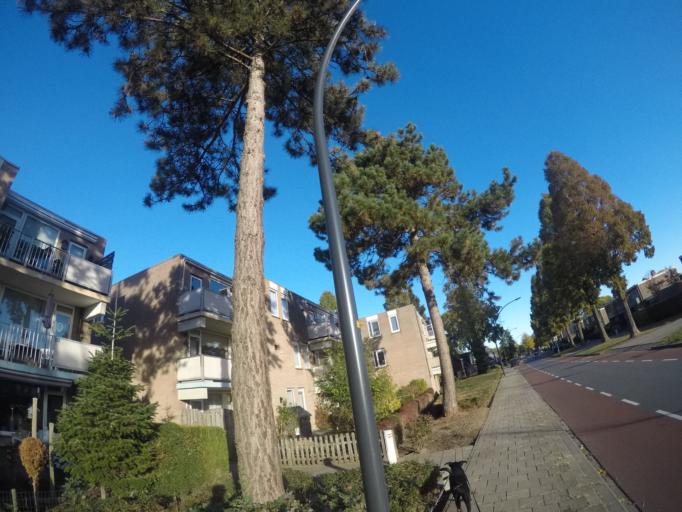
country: NL
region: Gelderland
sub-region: Gemeente Zevenaar
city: Zevenaar
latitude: 51.9294
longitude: 6.0811
